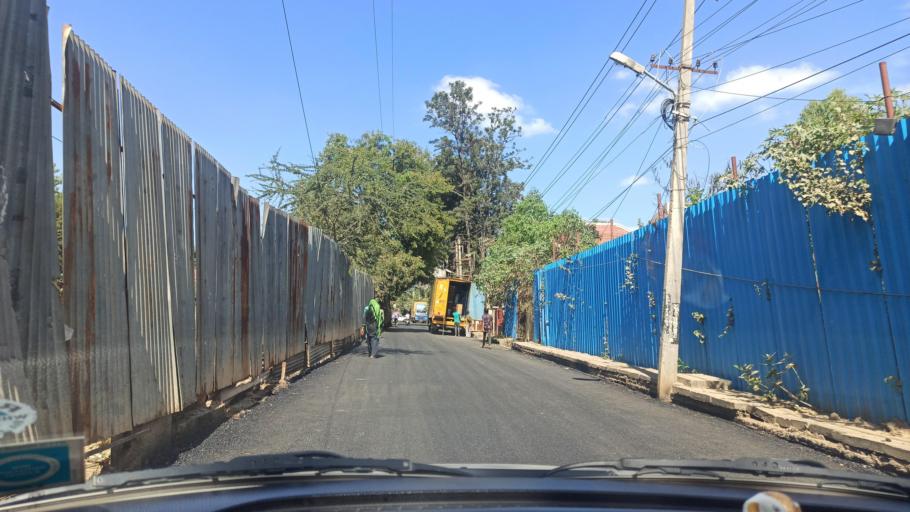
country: IN
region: Karnataka
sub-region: Bangalore Urban
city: Bangalore
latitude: 12.9329
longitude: 77.6861
